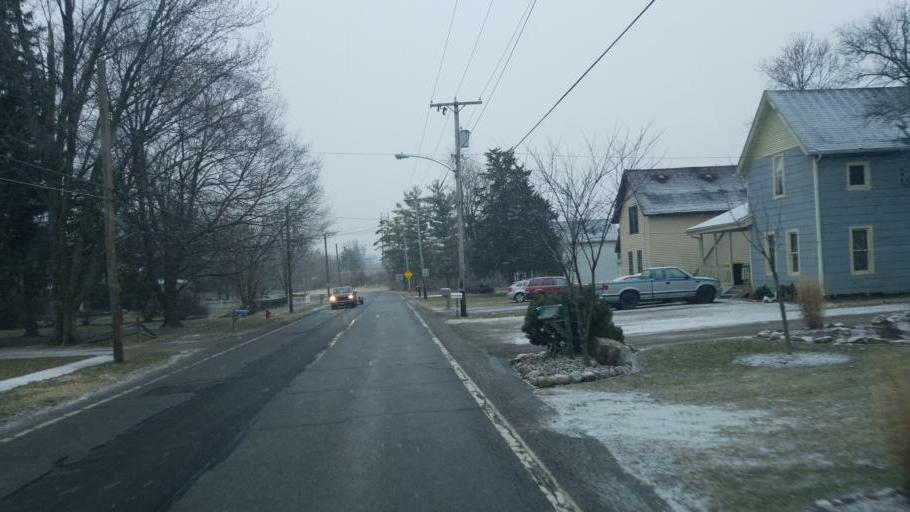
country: US
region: Ohio
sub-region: Defiance County
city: Hicksville
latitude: 41.2994
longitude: -84.7717
